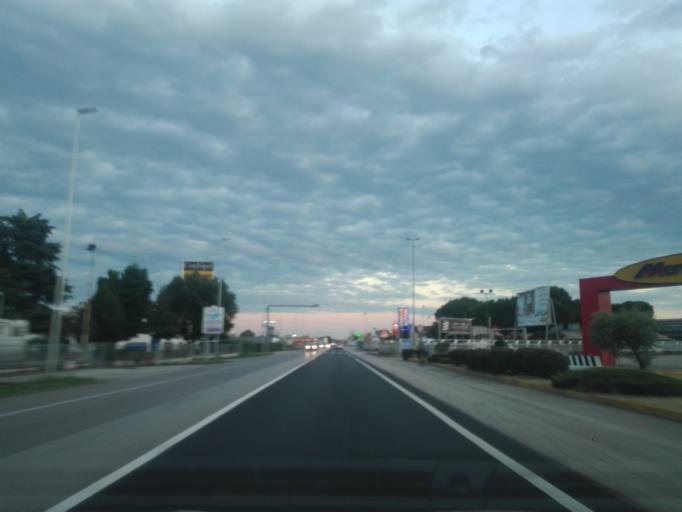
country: IT
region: Veneto
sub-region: Provincia di Rovigo
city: Santa Maria Maddalena
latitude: 44.9155
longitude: 11.5983
